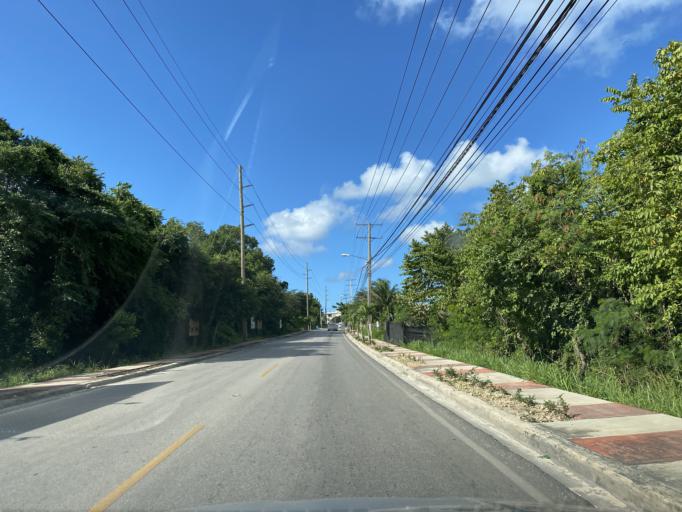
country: DO
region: La Romana
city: La Romana
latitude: 18.3709
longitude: -68.8320
